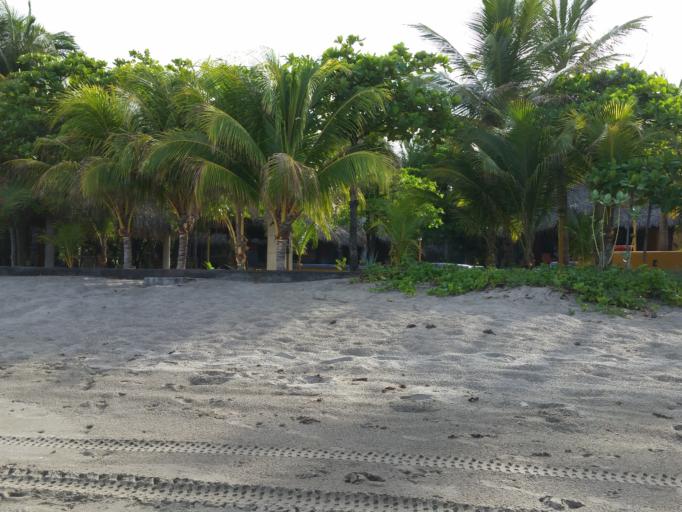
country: NI
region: Managua
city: Masachapa
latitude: 11.7794
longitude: -86.5179
